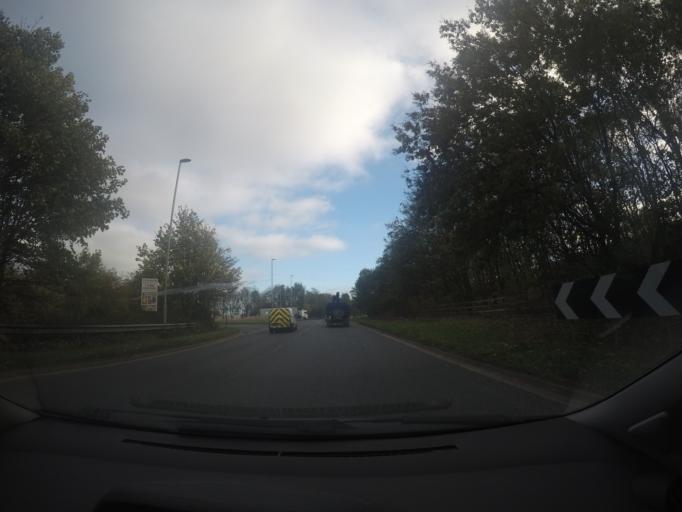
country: GB
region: England
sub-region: City and Borough of Leeds
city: Leeds
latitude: 53.7697
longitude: -1.5166
